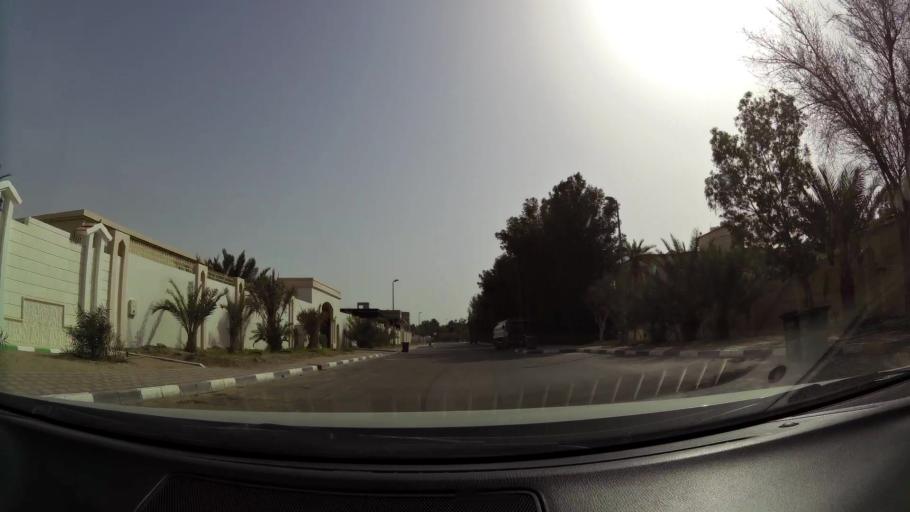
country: AE
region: Abu Dhabi
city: Al Ain
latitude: 24.1565
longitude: 55.7097
